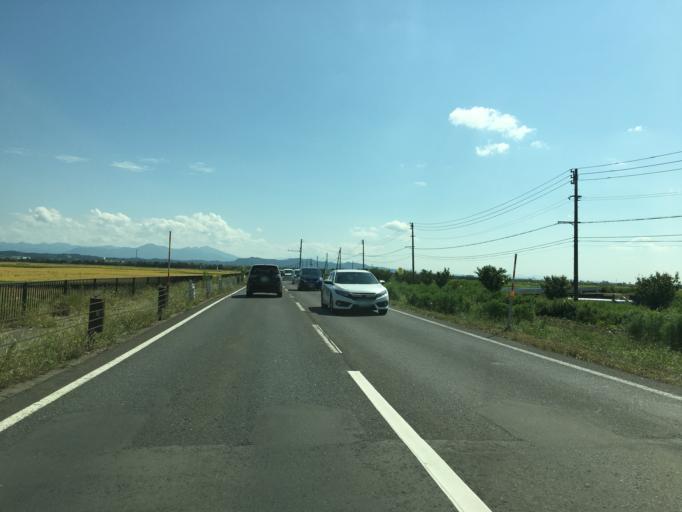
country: JP
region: Niigata
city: Niitsu-honcho
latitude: 37.8314
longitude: 139.0971
